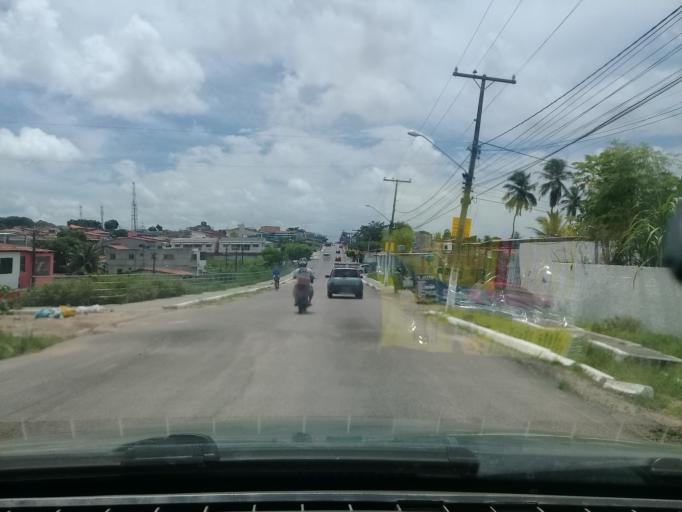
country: BR
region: Pernambuco
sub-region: Igarassu
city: Igarassu
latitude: -7.8465
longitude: -34.9086
